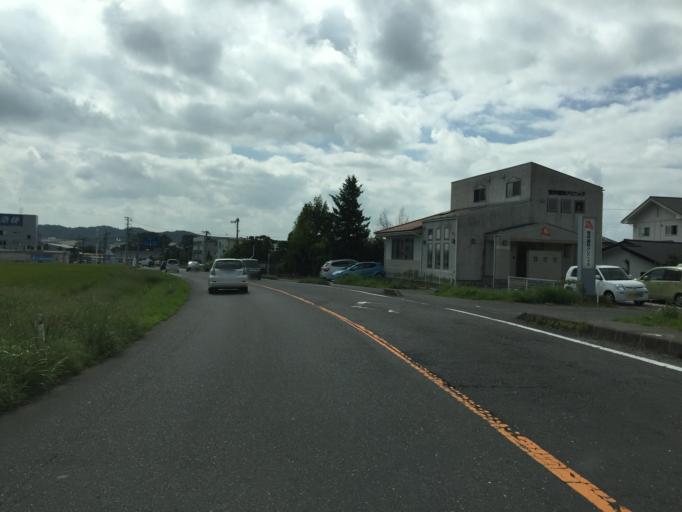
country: JP
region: Fukushima
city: Motomiya
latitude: 37.4885
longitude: 140.3720
